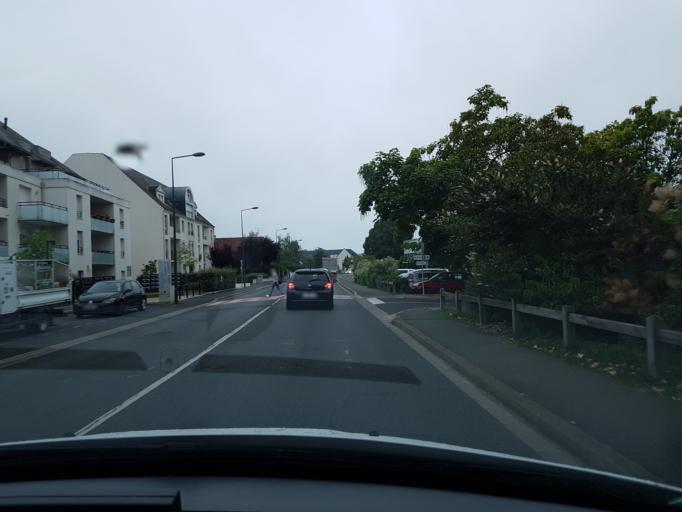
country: FR
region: Centre
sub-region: Departement d'Indre-et-Loire
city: Saint-Avertin
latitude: 47.3690
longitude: 0.7296
